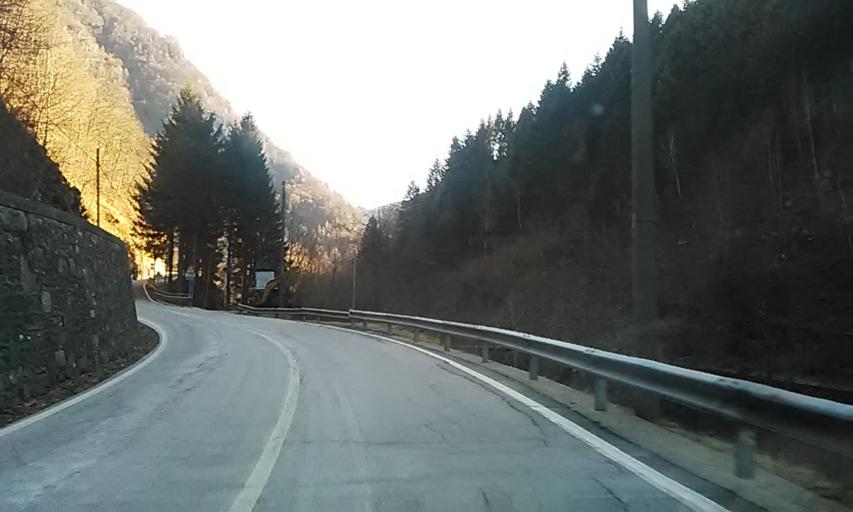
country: IT
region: Piedmont
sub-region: Provincia di Vercelli
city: Rimasco
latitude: 45.8415
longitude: 8.0784
